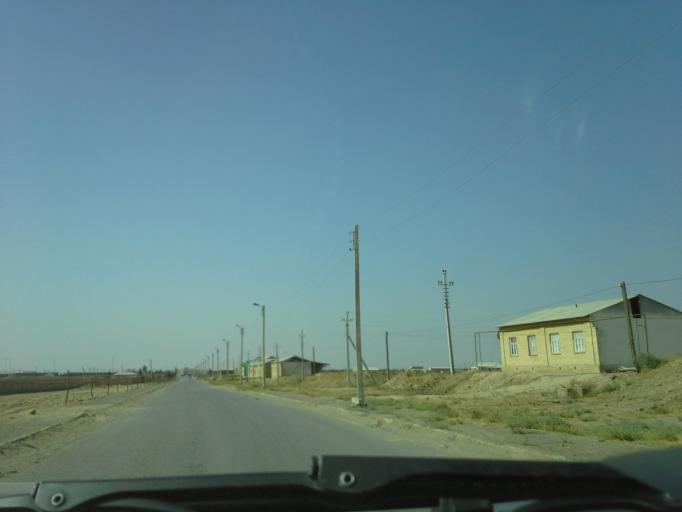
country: TM
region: Lebap
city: Atamyrat
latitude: 37.8215
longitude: 65.1835
